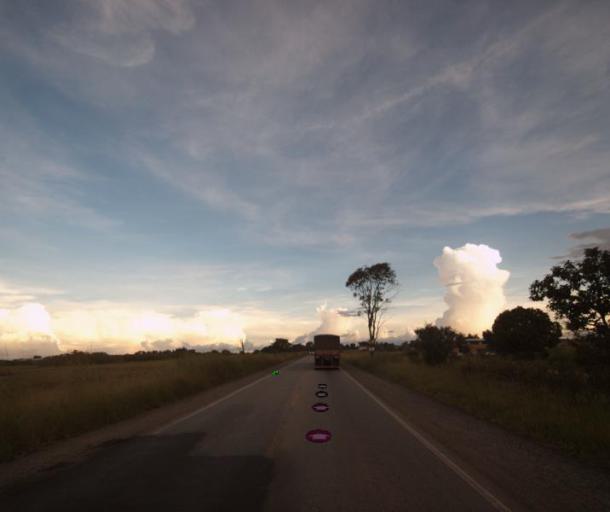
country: BR
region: Goias
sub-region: Uruacu
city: Uruacu
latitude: -14.2962
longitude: -49.1495
